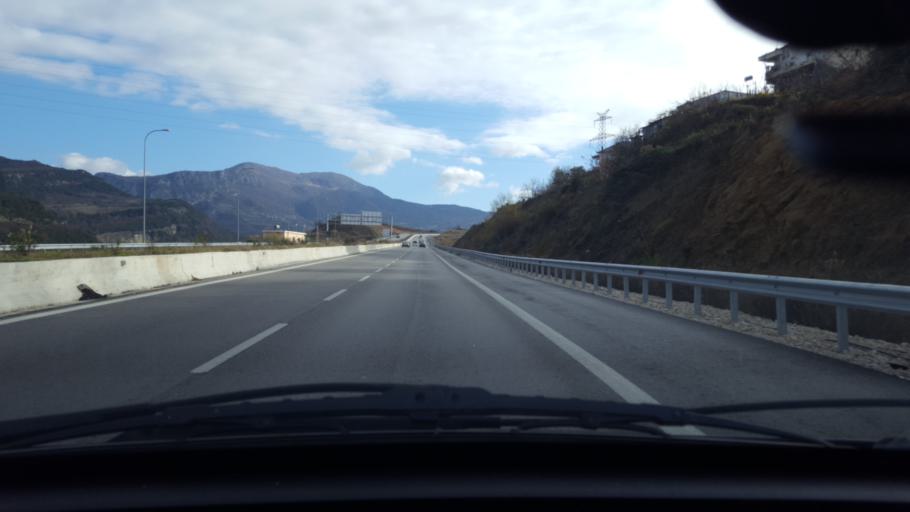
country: AL
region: Tirane
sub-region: Rrethi i Tiranes
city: Berzhite
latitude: 41.2267
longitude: 19.9342
